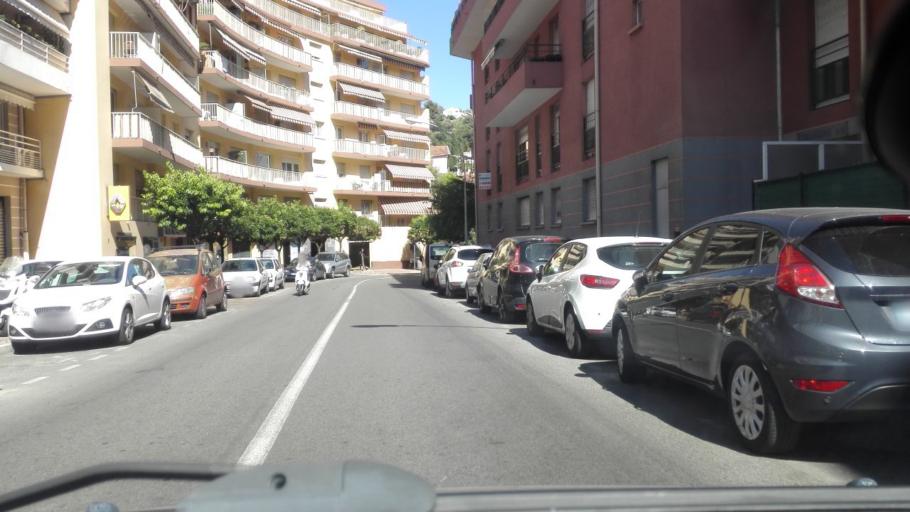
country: FR
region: Provence-Alpes-Cote d'Azur
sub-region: Departement des Alpes-Maritimes
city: Roquebrune-Cap-Martin
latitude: 43.7790
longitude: 7.4839
